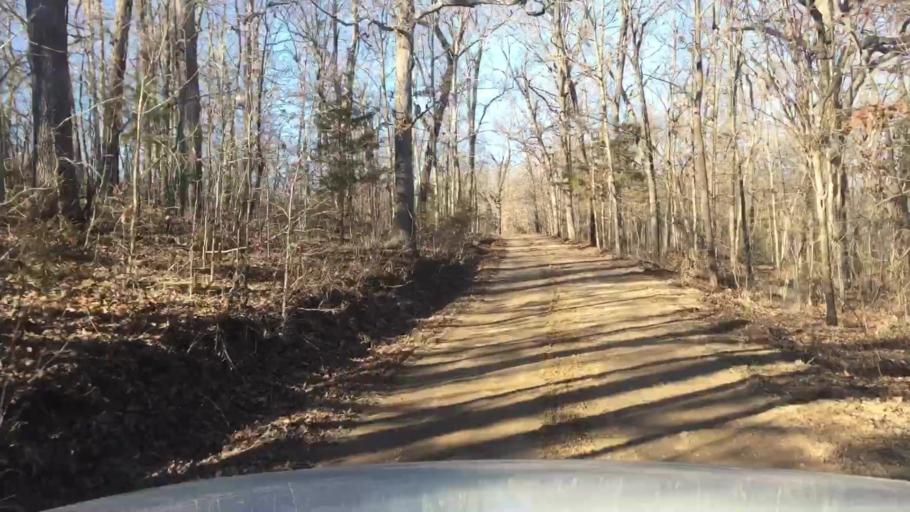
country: US
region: Missouri
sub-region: Camden County
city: Four Seasons
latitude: 38.3151
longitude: -92.7543
